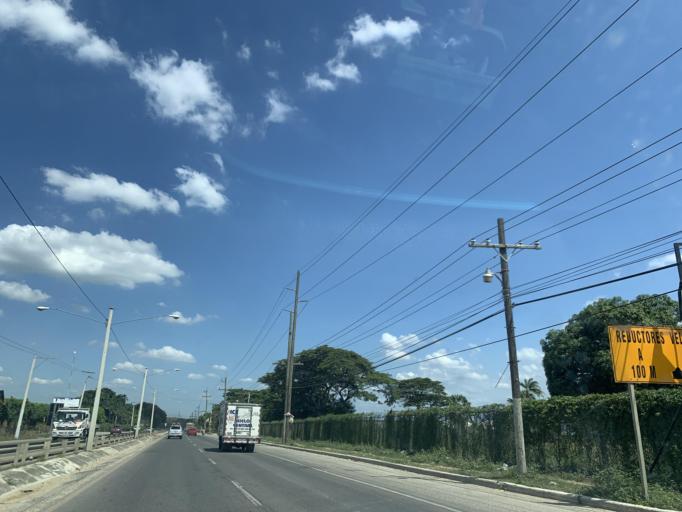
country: DO
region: Santiago
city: Villa Bisono
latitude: 19.5522
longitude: -70.8578
